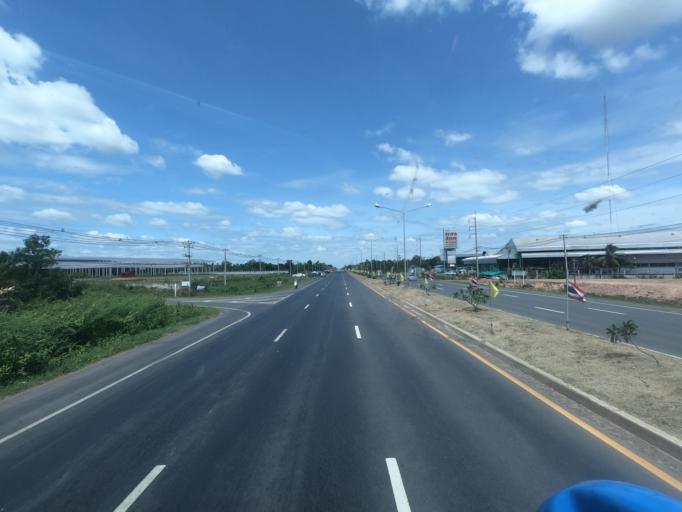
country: TH
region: Surin
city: Prasat
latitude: 14.6286
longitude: 103.4008
